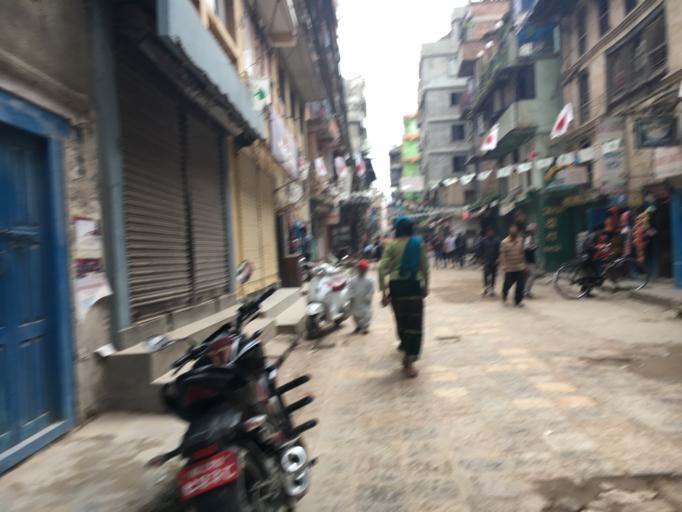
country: NP
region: Central Region
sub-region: Bagmati Zone
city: Kathmandu
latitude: 27.7086
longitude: 85.3104
